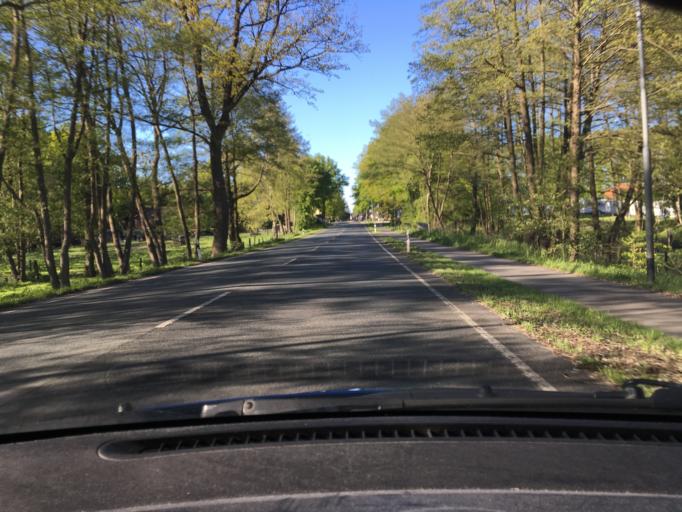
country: DE
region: Lower Saxony
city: Schneverdingen
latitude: 53.0700
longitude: 9.8620
